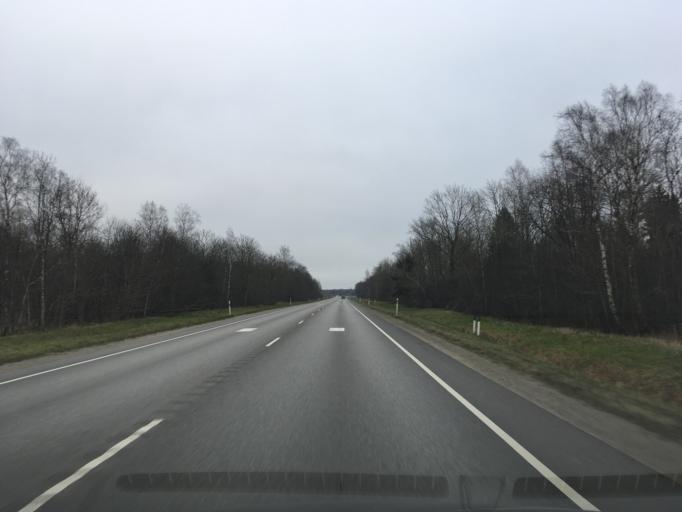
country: EE
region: Ida-Virumaa
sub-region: Kohtla-Jaerve linn
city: Kohtla-Jarve
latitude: 59.4207
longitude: 27.2607
